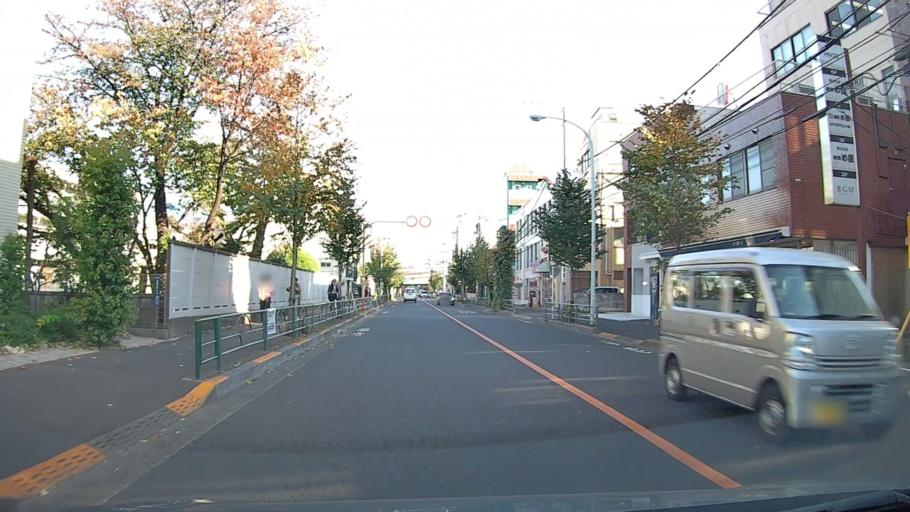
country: JP
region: Tokyo
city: Musashino
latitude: 35.7040
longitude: 139.5736
